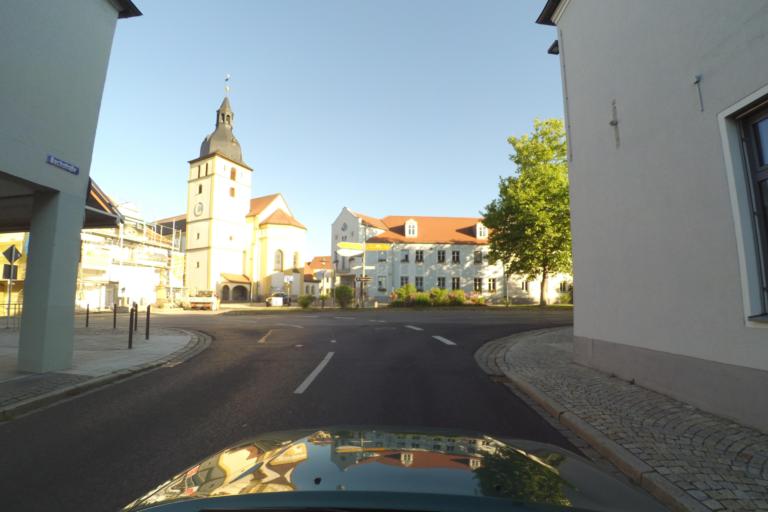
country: DE
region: Bavaria
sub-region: Upper Palatinate
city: Mitterteich
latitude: 49.9510
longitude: 12.2441
